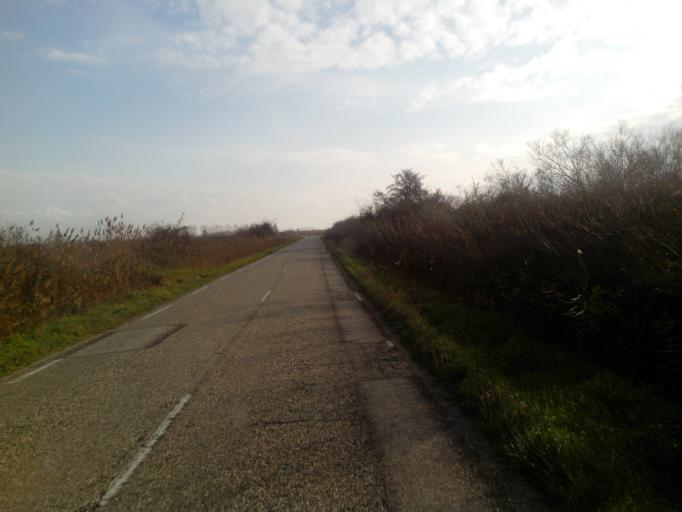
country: FR
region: Languedoc-Roussillon
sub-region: Departement du Gard
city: Saint-Gilles
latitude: 43.5929
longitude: 4.4924
